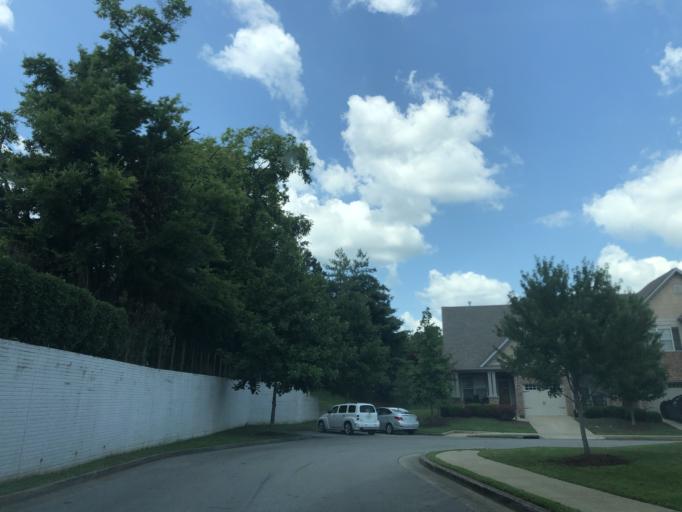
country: US
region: Tennessee
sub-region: Davidson County
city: Lakewood
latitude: 36.2188
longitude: -86.5967
